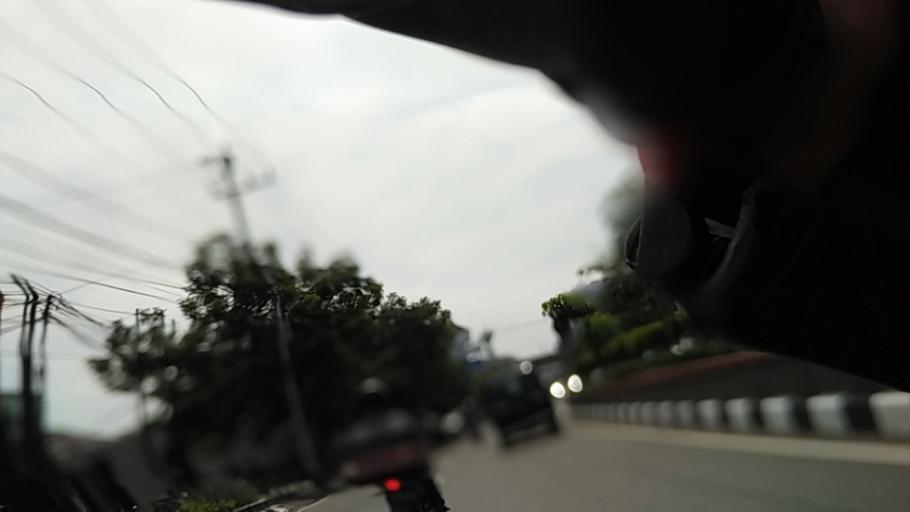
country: ID
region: Central Java
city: Semarang
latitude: -6.9876
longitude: 110.4177
